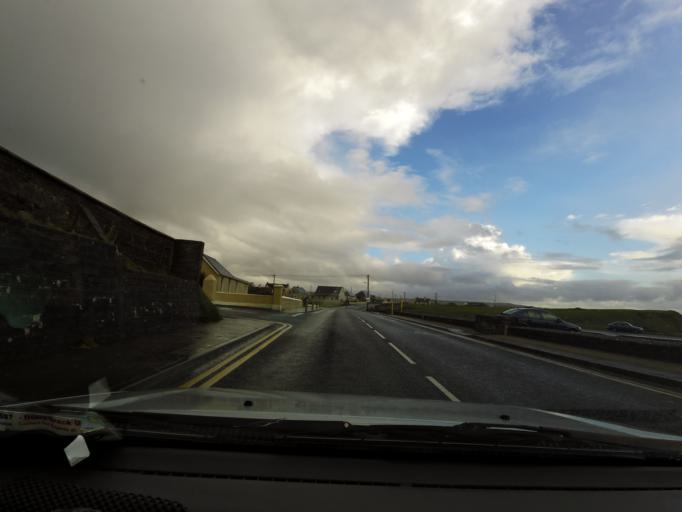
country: IE
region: Munster
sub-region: An Clar
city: Kilrush
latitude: 52.9297
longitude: -9.3463
